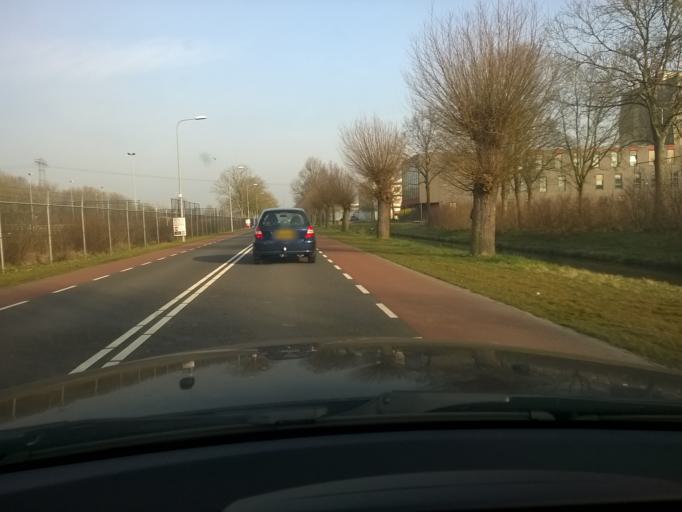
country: NL
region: Groningen
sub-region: Gemeente Groningen
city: Korrewegwijk
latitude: 53.2383
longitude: 6.5312
